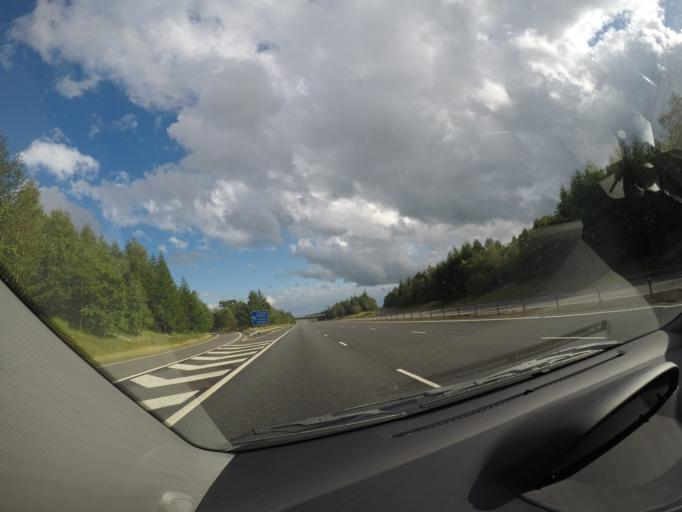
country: GB
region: Scotland
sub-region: Dumfries and Galloway
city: Lockerbie
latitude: 55.1362
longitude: -3.3700
